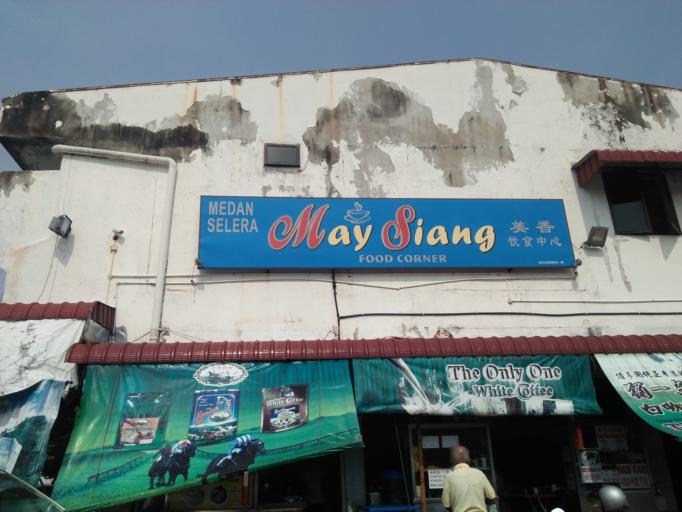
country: MY
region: Kedah
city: Kulim
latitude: 5.3709
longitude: 100.5569
